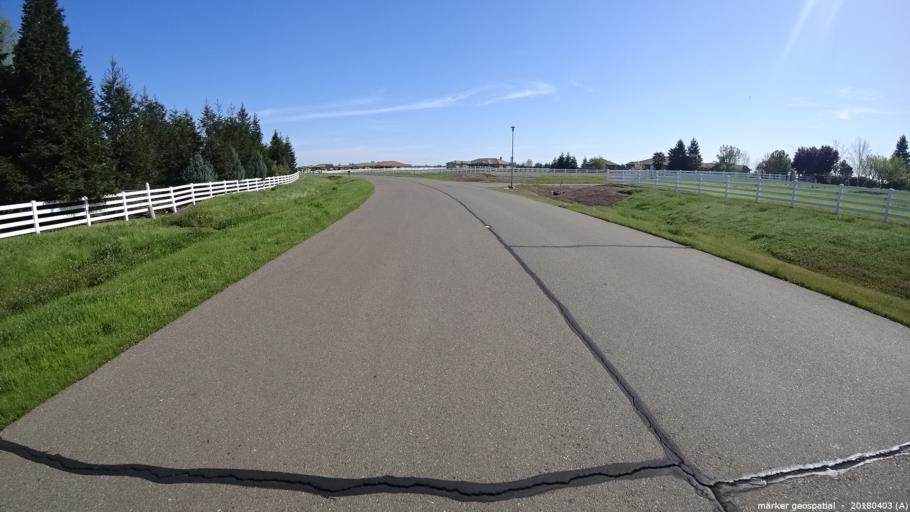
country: US
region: California
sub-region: Sacramento County
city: Wilton
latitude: 38.4150
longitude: -121.1992
